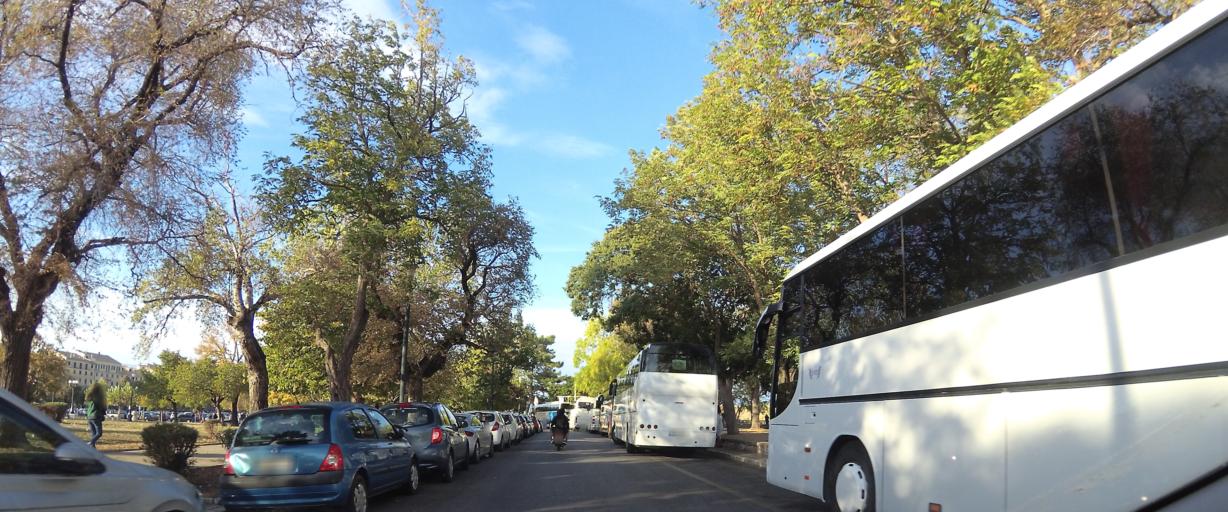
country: GR
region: Ionian Islands
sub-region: Nomos Kerkyras
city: Kerkyra
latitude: 39.6226
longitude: 19.9253
